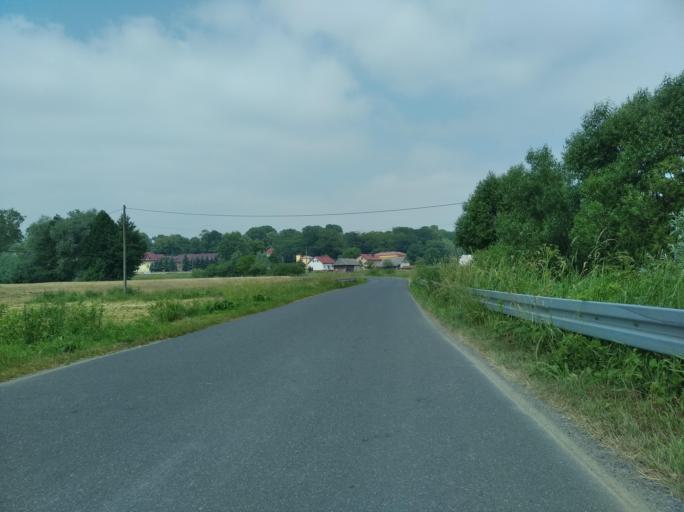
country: PL
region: Subcarpathian Voivodeship
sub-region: Powiat brzozowski
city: Haczow
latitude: 49.6302
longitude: 21.9231
